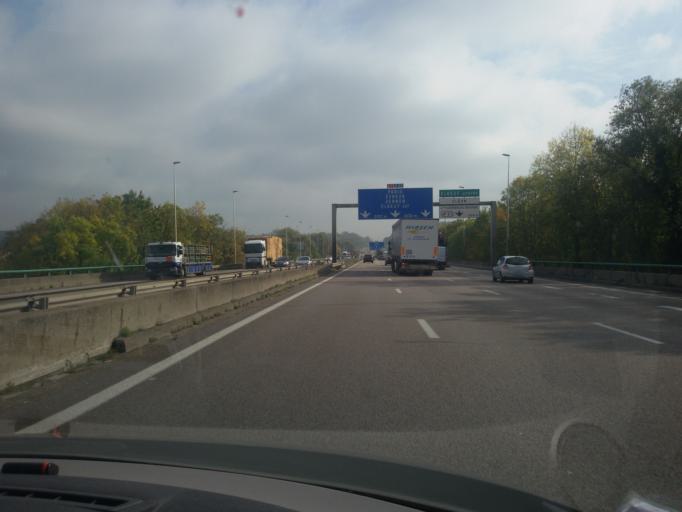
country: FR
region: Haute-Normandie
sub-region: Departement de la Seine-Maritime
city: Oissel
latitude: 49.3319
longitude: 1.0829
